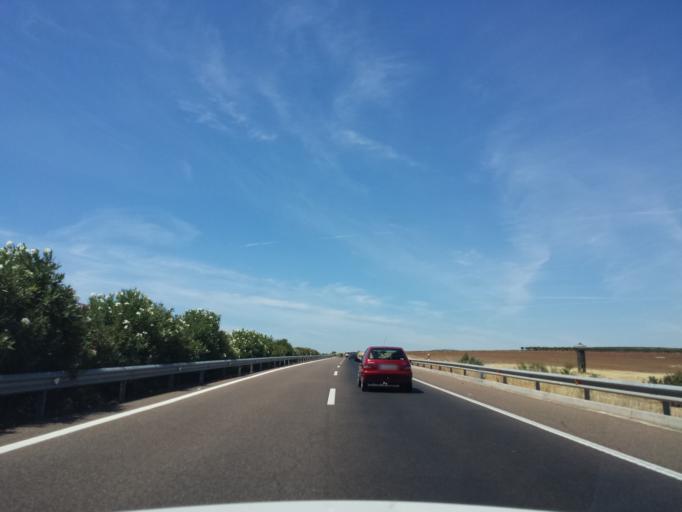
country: ES
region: Extremadura
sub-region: Provincia de Badajoz
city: Trujillanos
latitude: 38.9465
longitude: -6.2899
